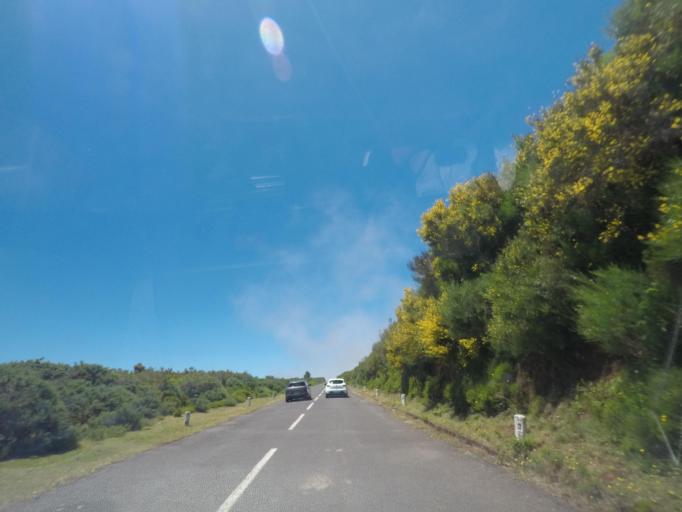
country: PT
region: Madeira
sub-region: Porto Moniz
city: Porto Moniz
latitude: 32.8044
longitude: -17.1911
